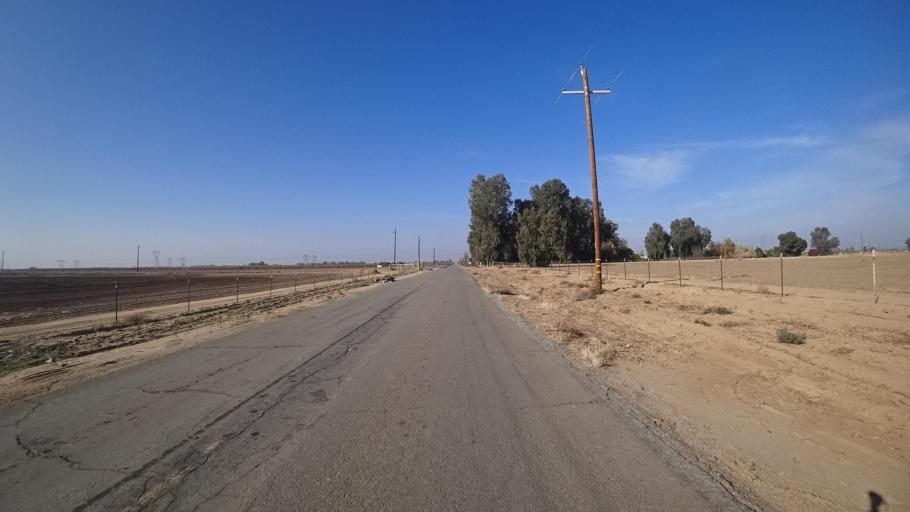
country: US
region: California
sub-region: Kern County
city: Lamont
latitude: 35.3253
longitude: -118.9184
